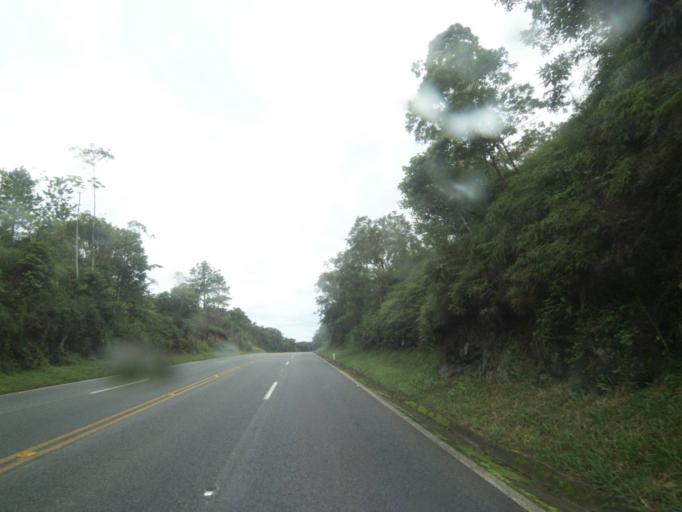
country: BR
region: Parana
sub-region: Pontal Do Parana
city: Pontal do Parana
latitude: -25.6815
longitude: -48.5768
